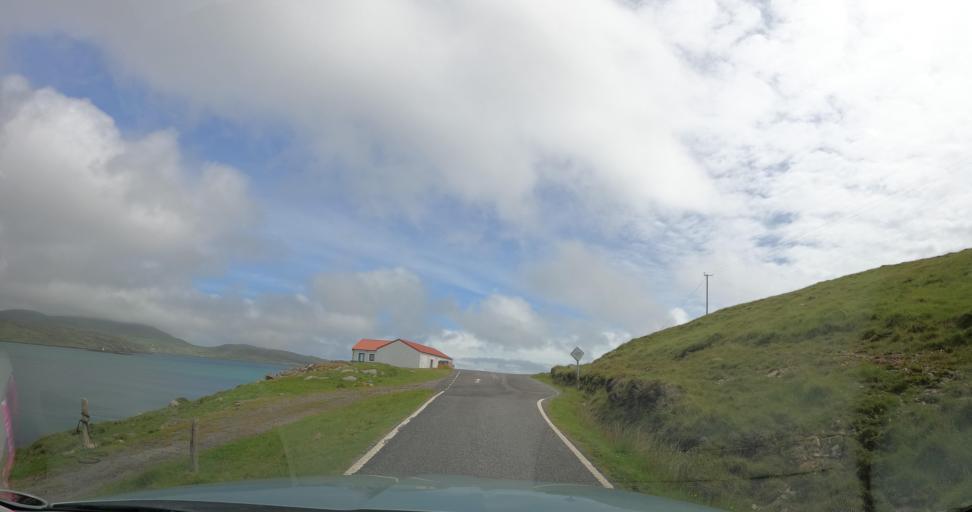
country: GB
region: Scotland
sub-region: Eilean Siar
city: Barra
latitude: 56.9371
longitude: -7.5251
